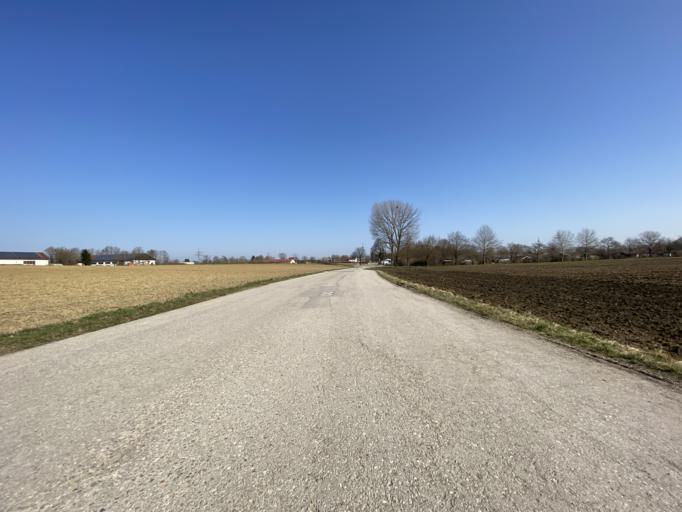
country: DE
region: Bavaria
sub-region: Upper Bavaria
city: Unterfoehring
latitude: 48.1961
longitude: 11.6609
